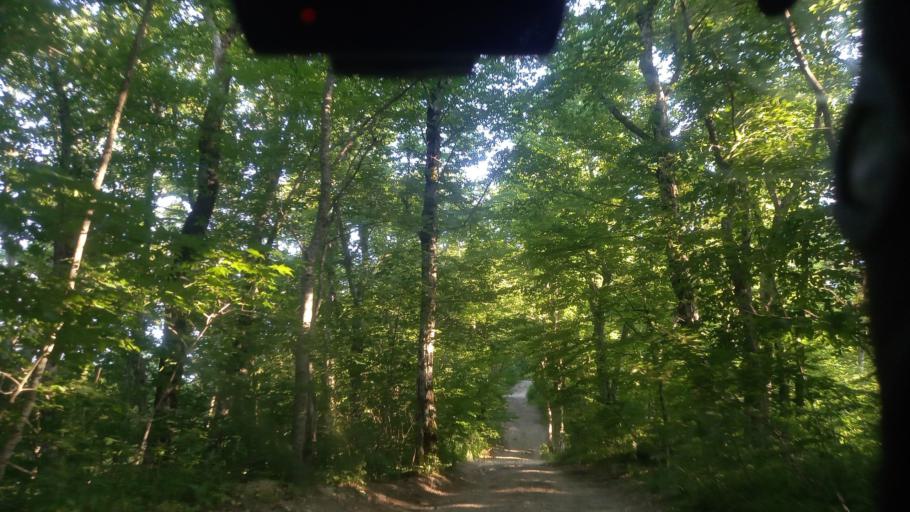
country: RU
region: Krasnodarskiy
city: Gelendzhik
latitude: 44.6251
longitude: 38.1889
